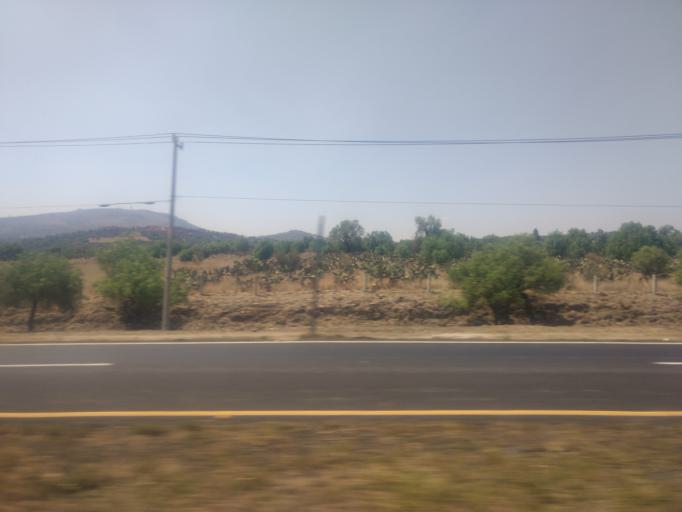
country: MX
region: Morelos
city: Axapusco
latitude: 19.7373
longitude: -98.7706
